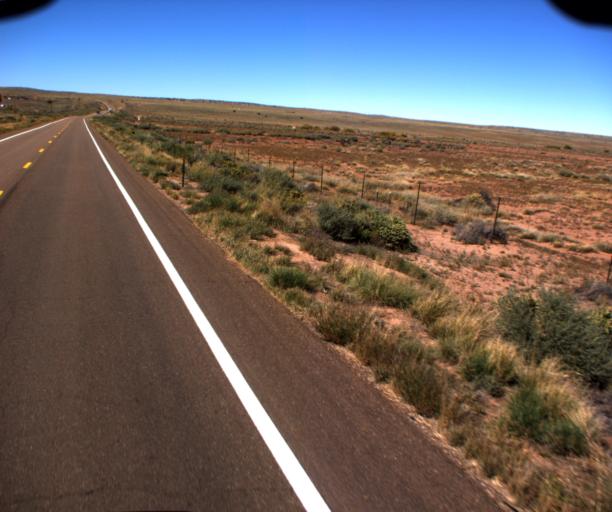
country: US
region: Arizona
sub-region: Apache County
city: Saint Johns
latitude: 34.5085
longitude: -109.4324
